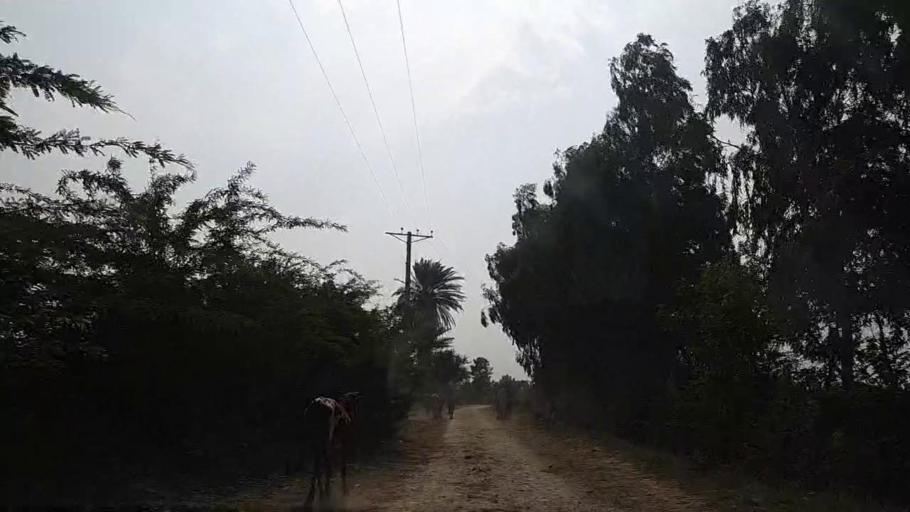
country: PK
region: Sindh
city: Mirpur Sakro
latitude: 24.6210
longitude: 67.7438
